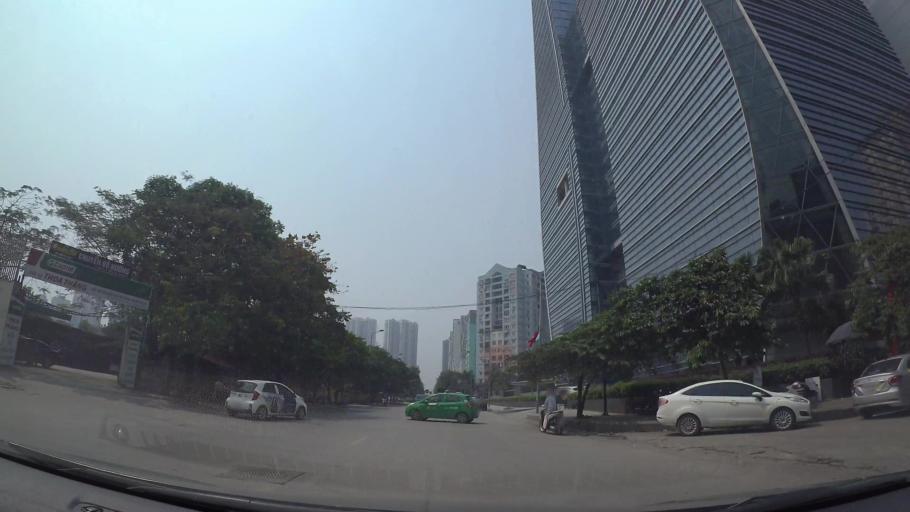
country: VN
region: Ha Noi
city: Thanh Xuan
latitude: 21.0013
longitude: 105.8011
